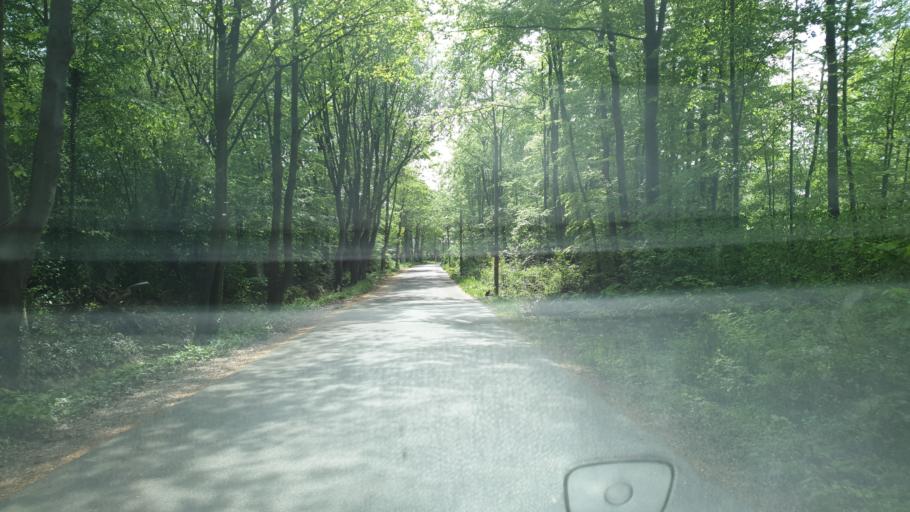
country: DE
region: North Rhine-Westphalia
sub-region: Regierungsbezirk Koln
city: Bergheim
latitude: 50.9382
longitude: 6.6987
